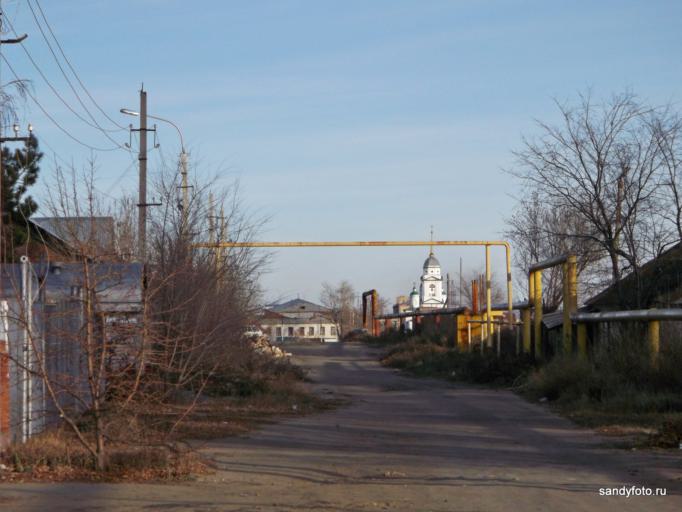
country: RU
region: Chelyabinsk
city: Troitsk
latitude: 54.0739
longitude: 61.5422
